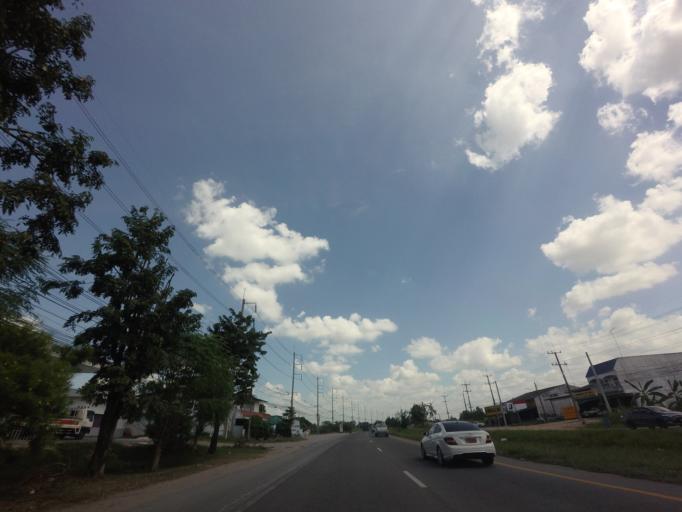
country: TH
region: Chon Buri
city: Ban Bueng
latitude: 13.2988
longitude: 101.1576
